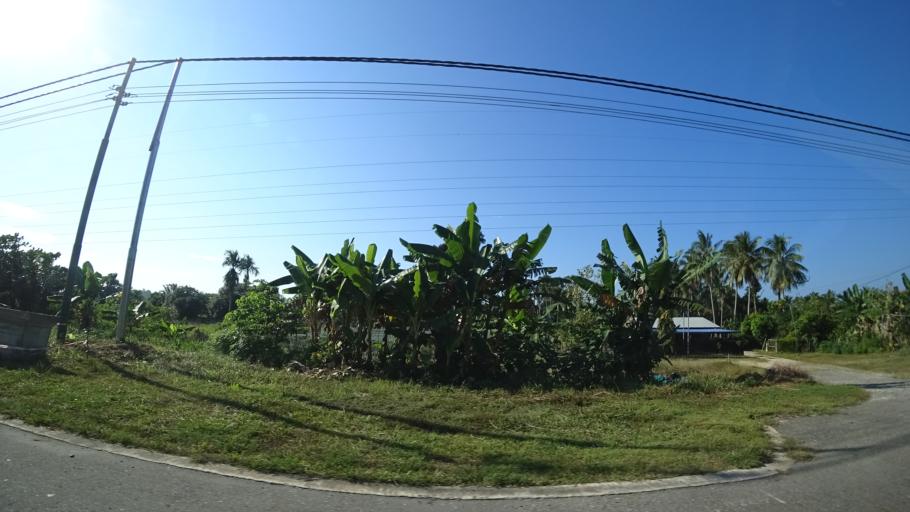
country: BN
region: Tutong
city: Tutong
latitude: 4.7065
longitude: 114.5289
